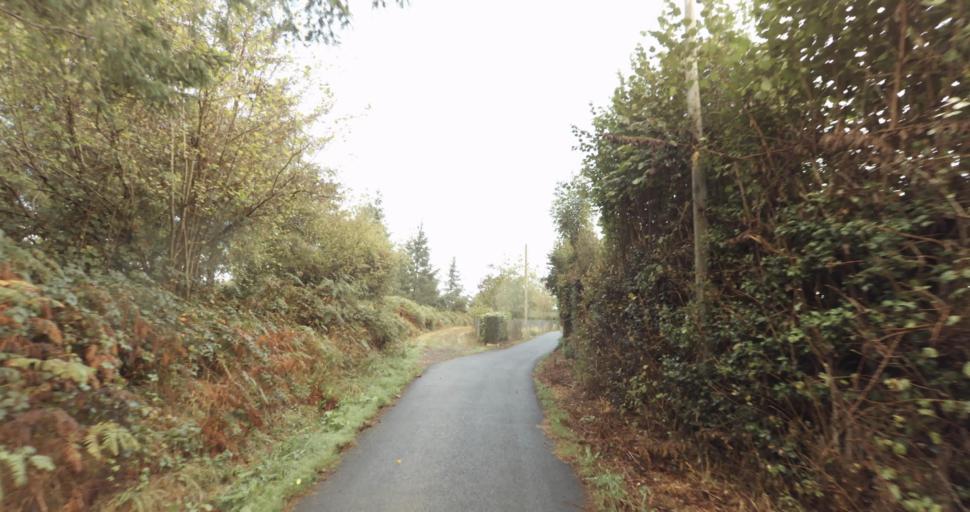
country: FR
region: Lower Normandy
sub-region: Departement de l'Orne
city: Vimoutiers
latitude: 48.9033
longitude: 0.2461
